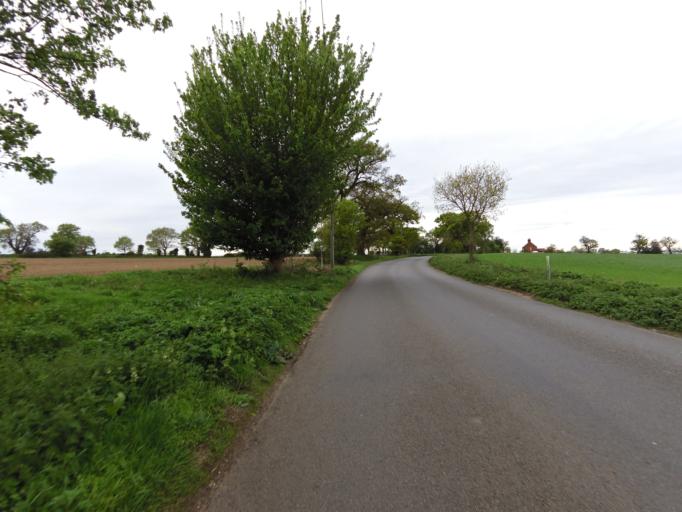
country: GB
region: England
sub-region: Suffolk
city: Kesgrave
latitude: 52.0179
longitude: 1.2191
